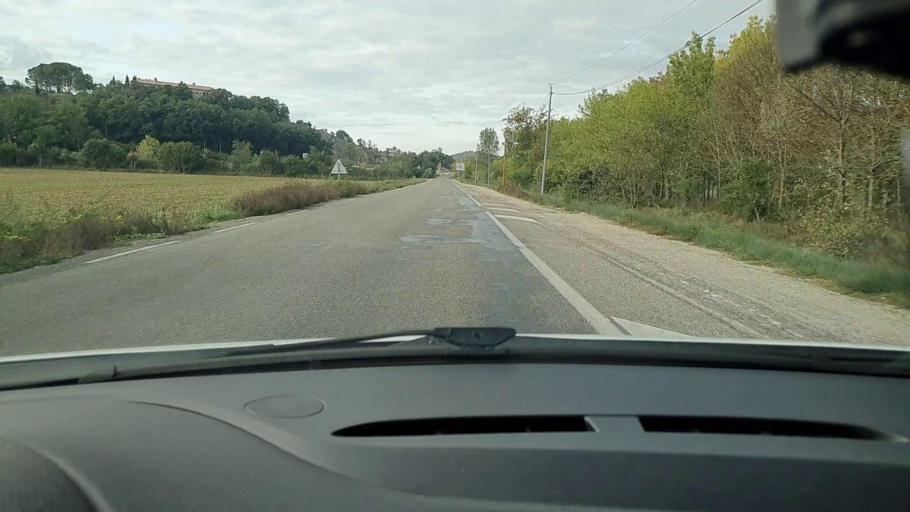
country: FR
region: Languedoc-Roussillon
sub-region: Departement du Gard
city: Saint-Ambroix
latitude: 44.2074
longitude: 4.2522
